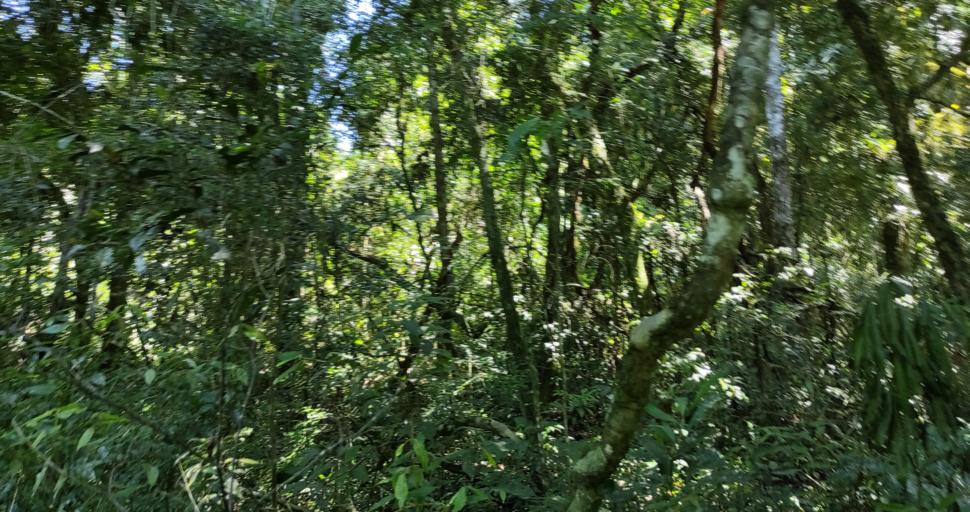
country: BR
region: Rio Grande do Sul
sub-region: Tres Passos
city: Tres Passos
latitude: -27.1506
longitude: -53.8988
